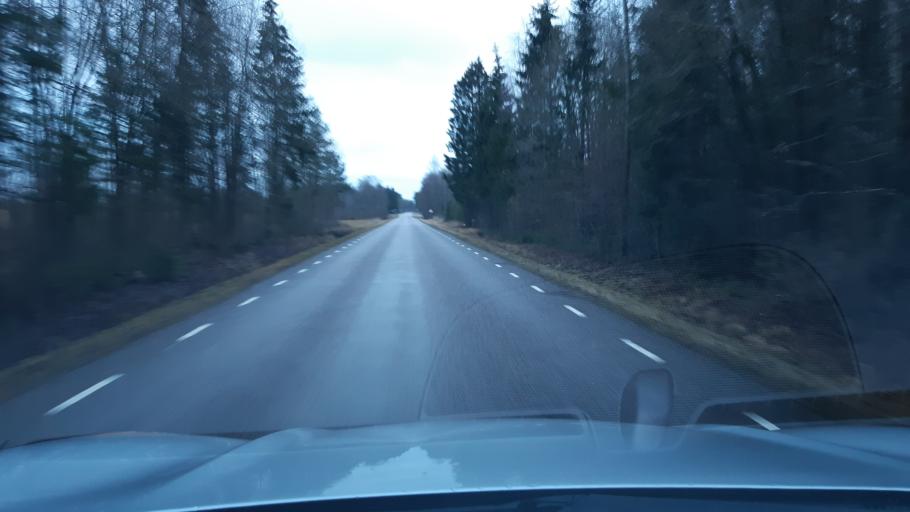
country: EE
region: Raplamaa
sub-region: Kohila vald
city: Kohila
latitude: 59.0808
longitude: 24.6770
